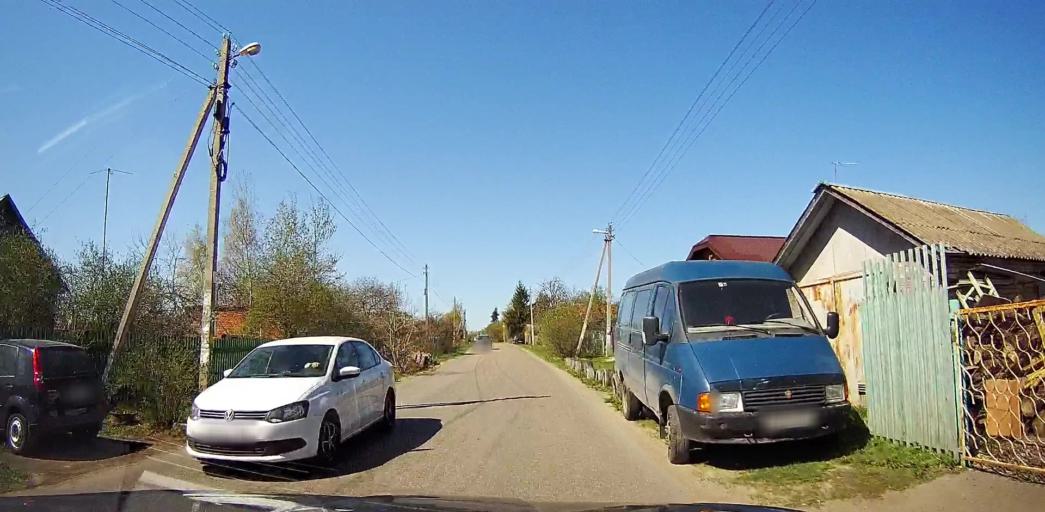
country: RU
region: Moskovskaya
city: Malyshevo
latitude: 55.4570
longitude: 38.3723
